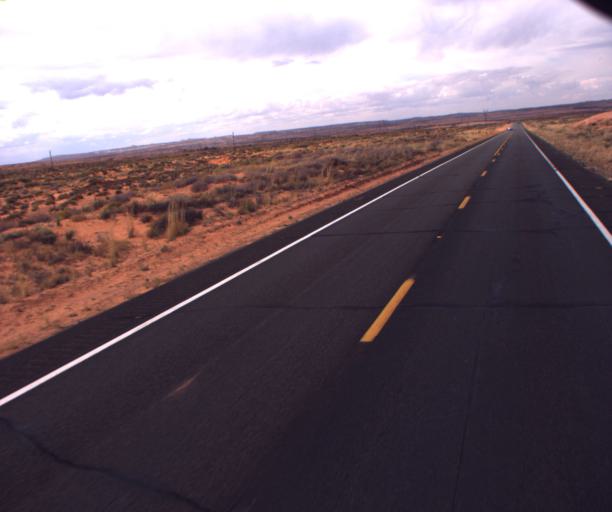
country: US
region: Arizona
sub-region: Apache County
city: Many Farms
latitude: 36.9333
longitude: -109.6293
